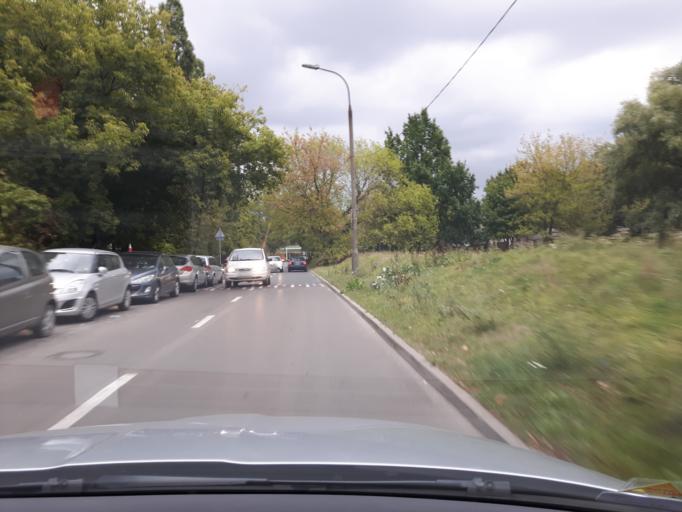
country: PL
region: Masovian Voivodeship
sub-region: Warszawa
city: Mokotow
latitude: 52.1687
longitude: 21.0225
